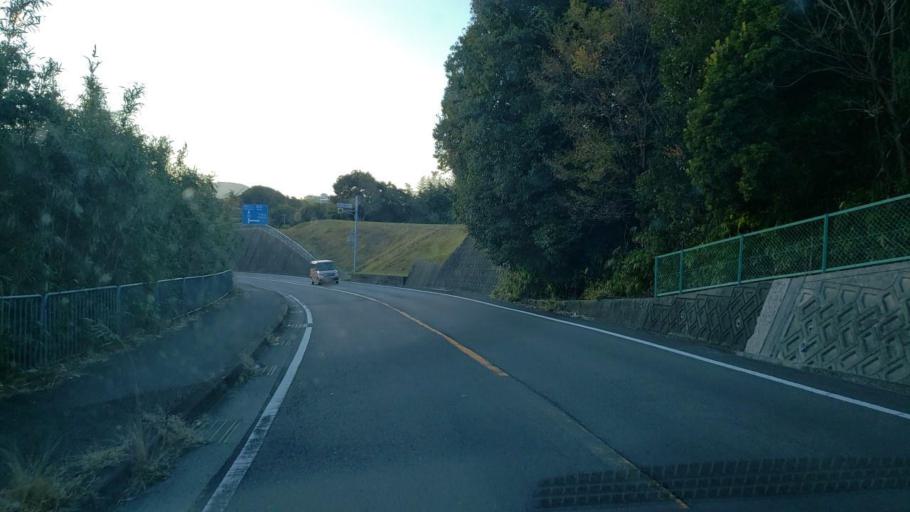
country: JP
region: Hyogo
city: Sumoto
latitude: 34.4404
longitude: 134.8822
